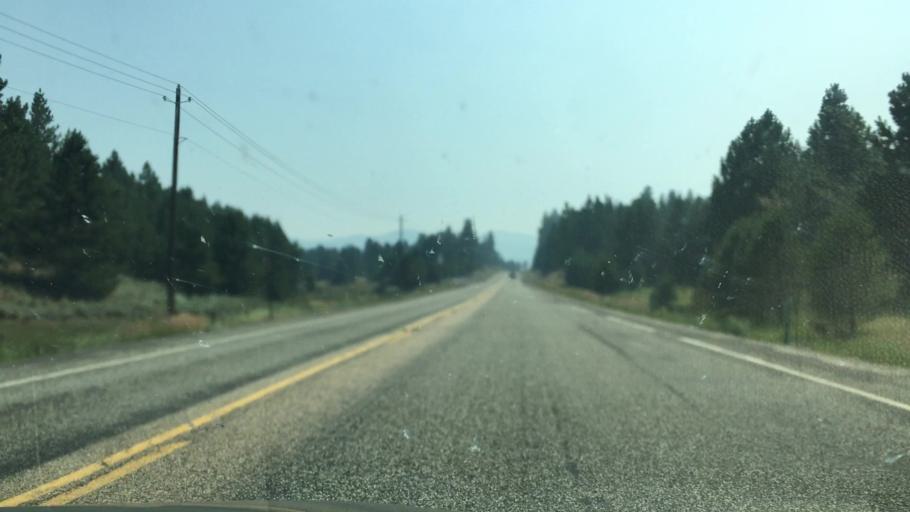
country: US
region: Idaho
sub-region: Valley County
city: Cascade
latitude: 44.3738
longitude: -116.0159
